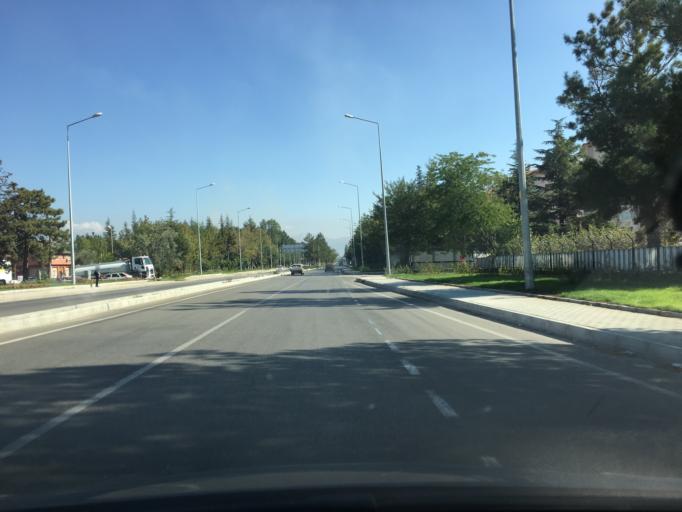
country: TR
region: Isparta
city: Isparta
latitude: 37.7842
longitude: 30.5684
